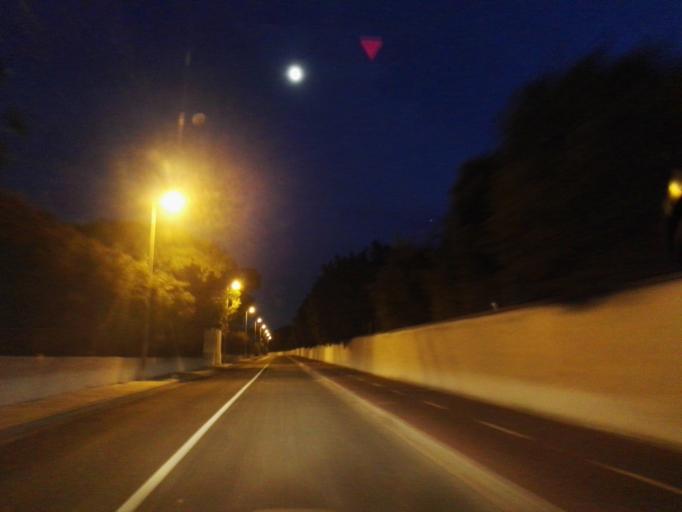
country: PT
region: Lisbon
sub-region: Cascais
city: Cascais
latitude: 38.7197
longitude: -9.4652
